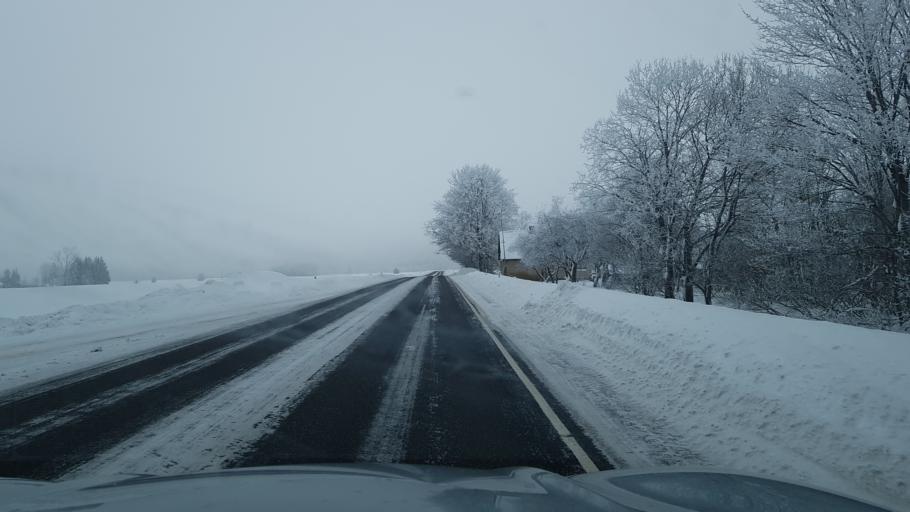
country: EE
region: Ida-Virumaa
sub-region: Johvi vald
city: Johvi
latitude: 59.2619
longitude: 27.3839
